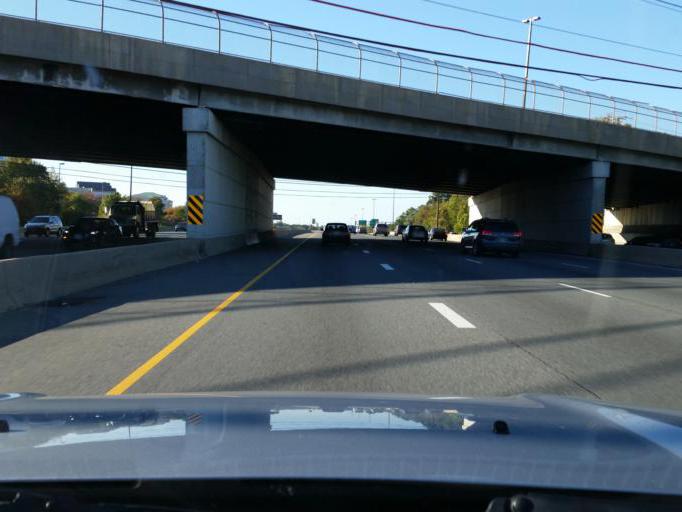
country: US
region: Maryland
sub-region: Montgomery County
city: Derwood
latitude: 39.1103
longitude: -77.1871
